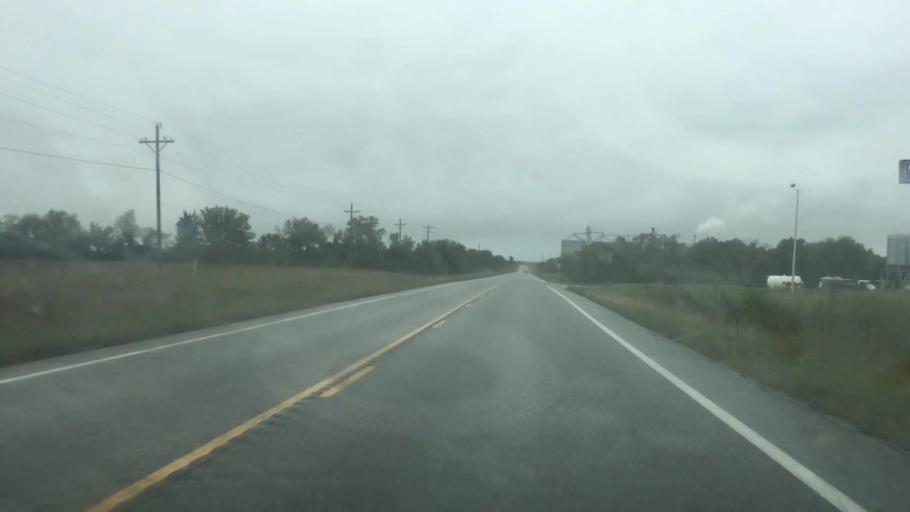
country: US
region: Kansas
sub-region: Anderson County
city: Garnett
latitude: 38.2772
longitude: -95.2269
